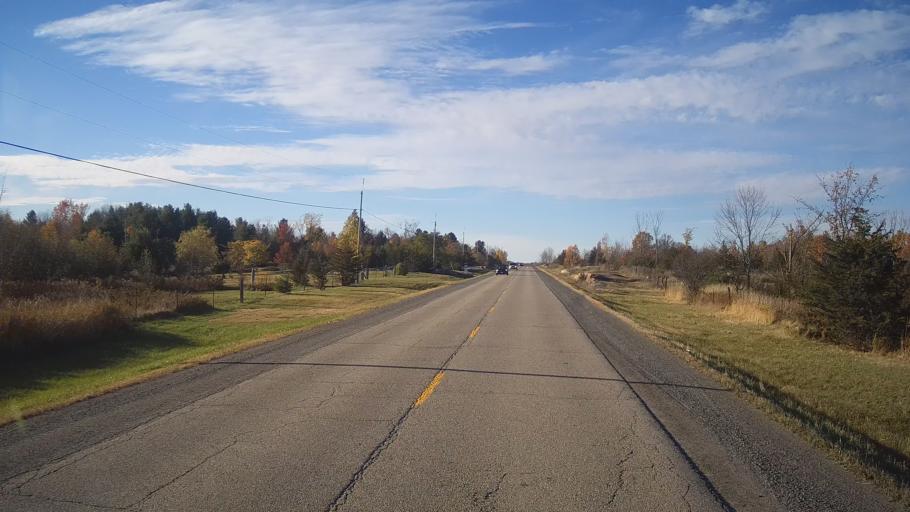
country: CA
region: Ontario
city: Perth
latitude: 44.7102
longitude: -76.4351
